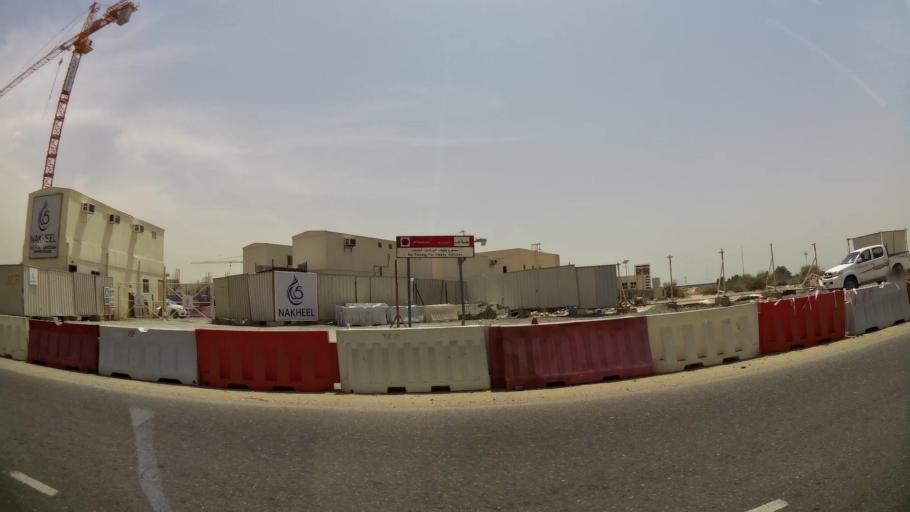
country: AE
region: Ash Shariqah
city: Sharjah
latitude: 25.1656
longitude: 55.3970
